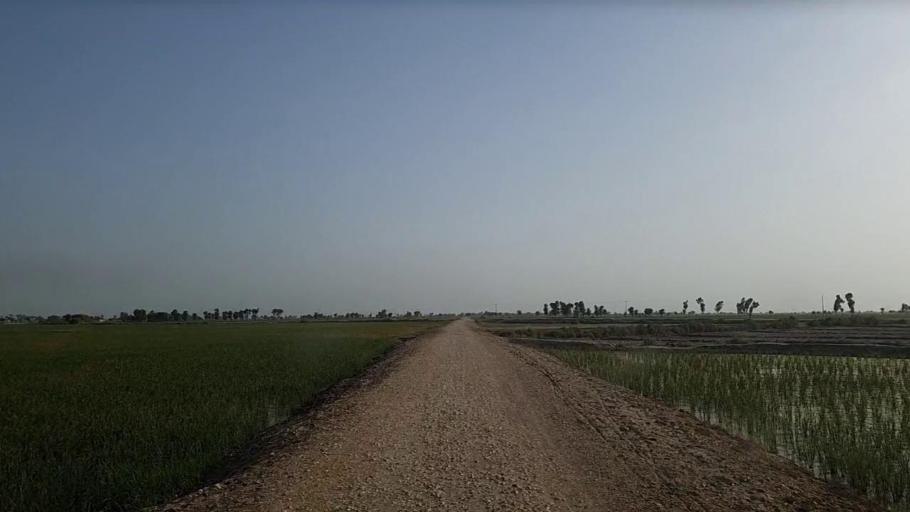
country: PK
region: Sindh
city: Sita Road
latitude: 27.1031
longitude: 67.8875
